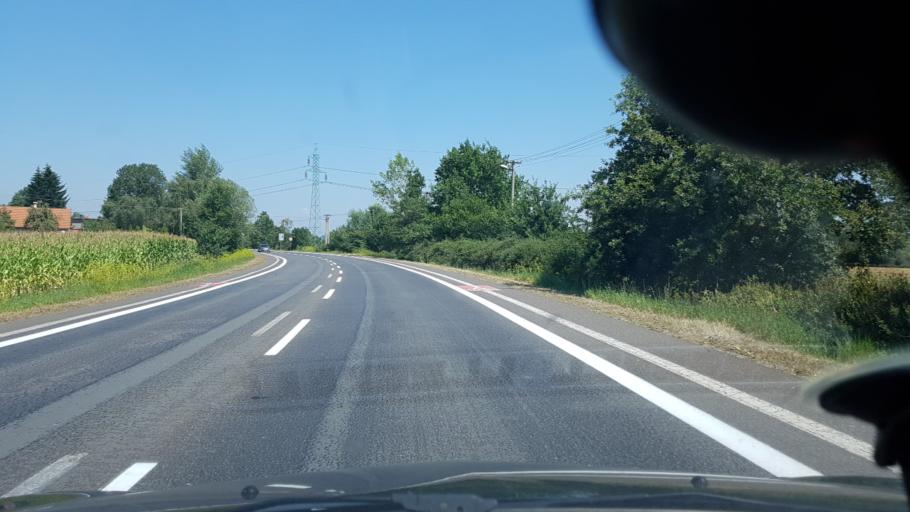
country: CZ
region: Moravskoslezsky
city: Stary Bohumin
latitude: 49.8998
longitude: 18.3350
